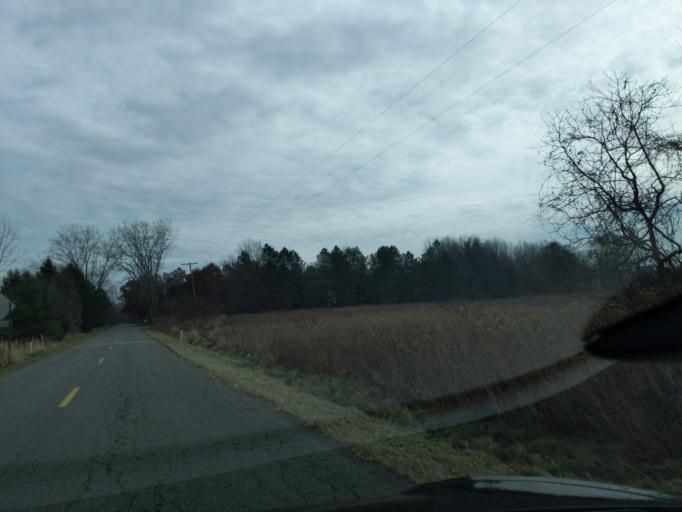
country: US
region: Michigan
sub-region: Ingham County
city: Leslie
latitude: 42.4649
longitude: -84.5150
